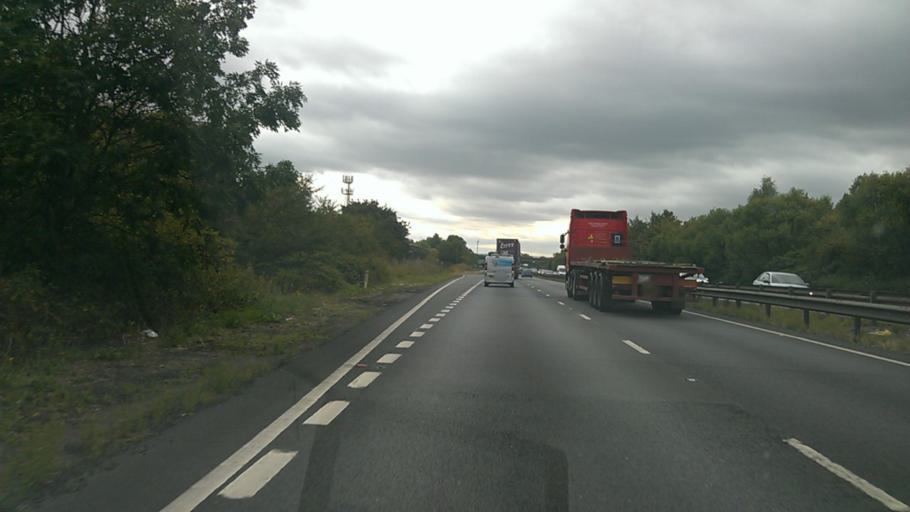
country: GB
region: England
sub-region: Cambridgeshire
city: Hemingford Grey
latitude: 52.3008
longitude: -0.0828
